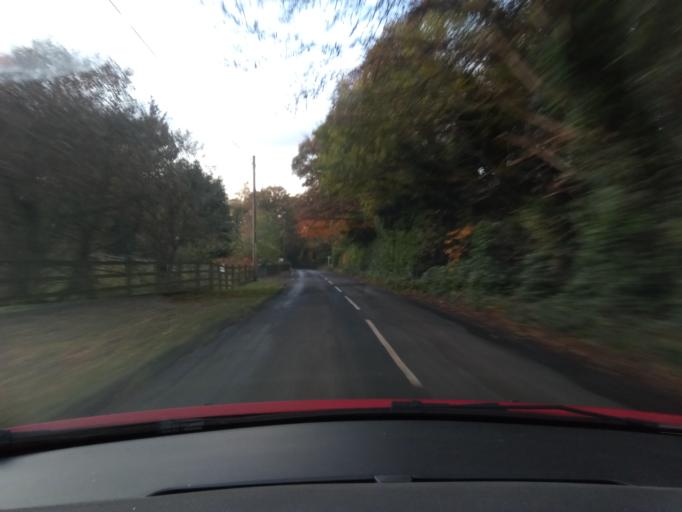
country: GB
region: England
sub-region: Northumberland
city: Bardon Mill
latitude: 54.9443
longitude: -2.2685
